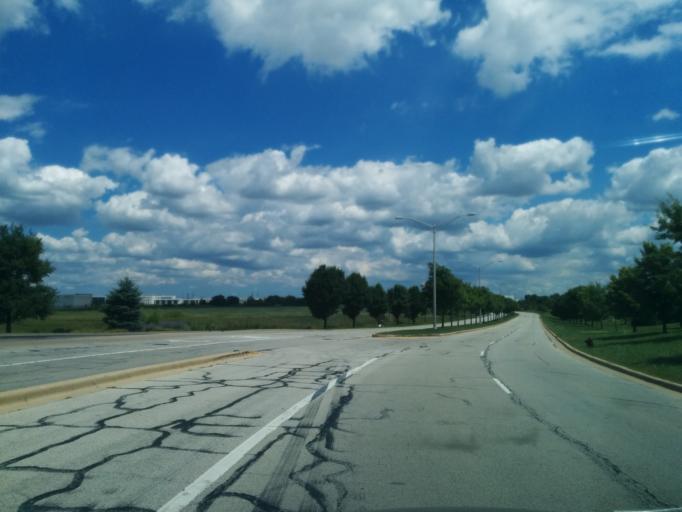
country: US
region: Illinois
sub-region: Will County
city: Romeoville
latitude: 41.6754
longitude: -88.1163
